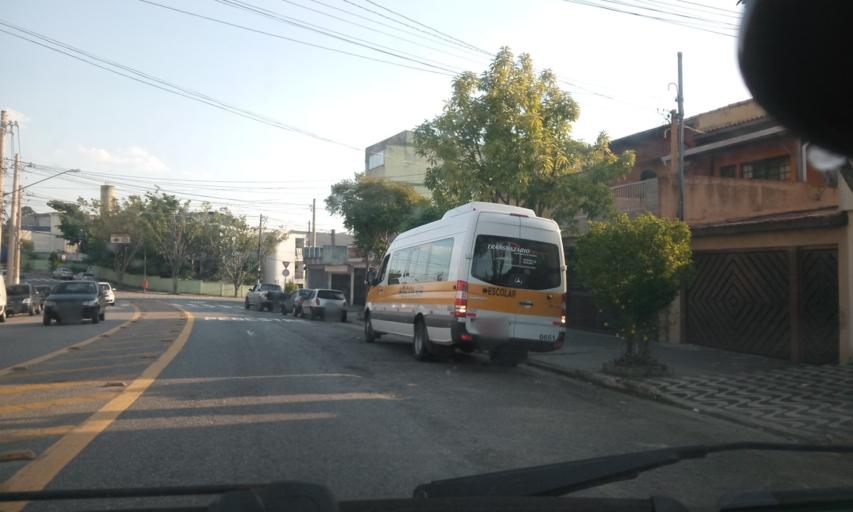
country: BR
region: Sao Paulo
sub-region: Sao Bernardo Do Campo
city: Sao Bernardo do Campo
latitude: -23.7474
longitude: -46.5485
